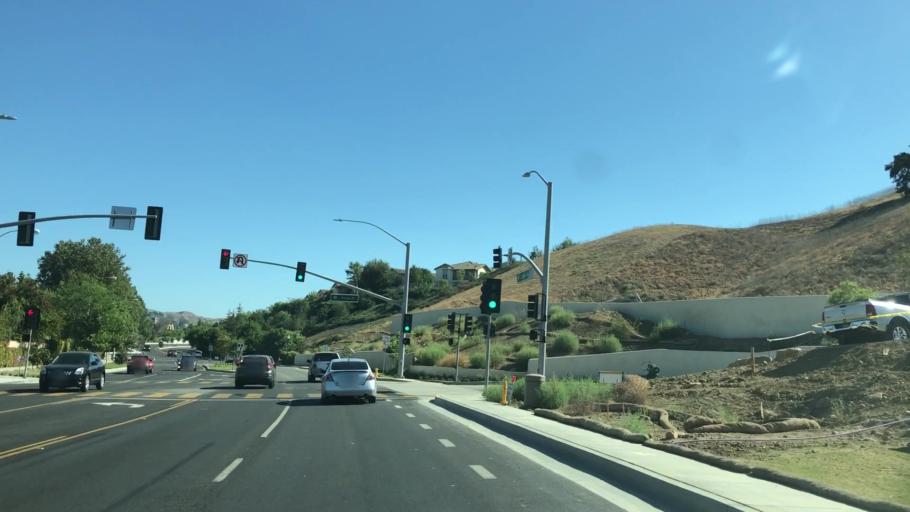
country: US
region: California
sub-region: Los Angeles County
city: Agoura
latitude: 34.1387
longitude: -118.7006
